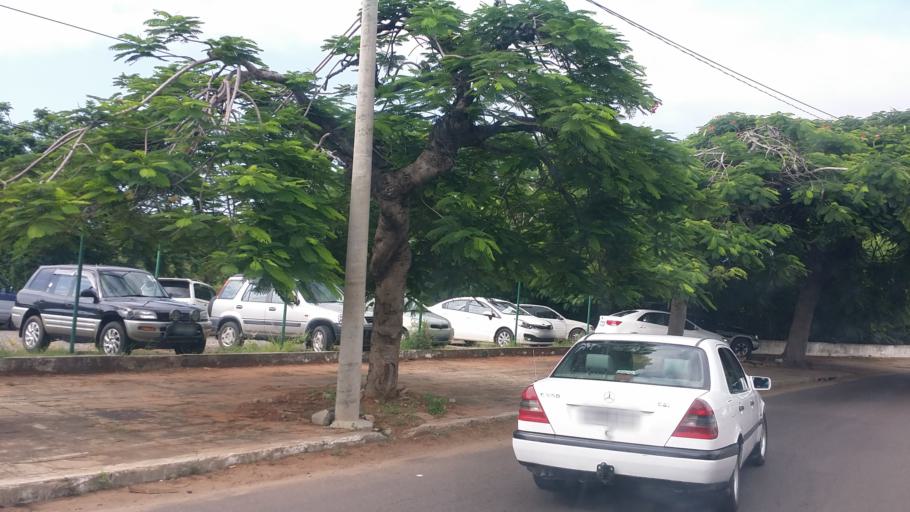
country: MZ
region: Maputo City
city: Maputo
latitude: -25.9812
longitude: 32.5924
